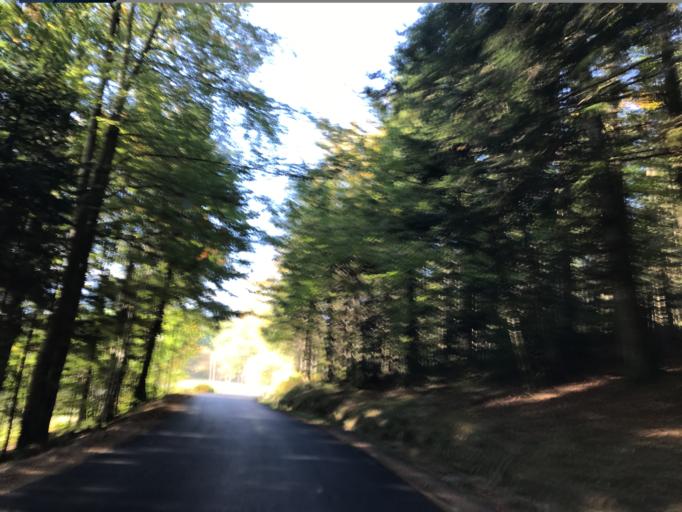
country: FR
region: Auvergne
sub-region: Departement du Puy-de-Dome
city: Celles-sur-Durolle
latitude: 45.8042
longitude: 3.6687
